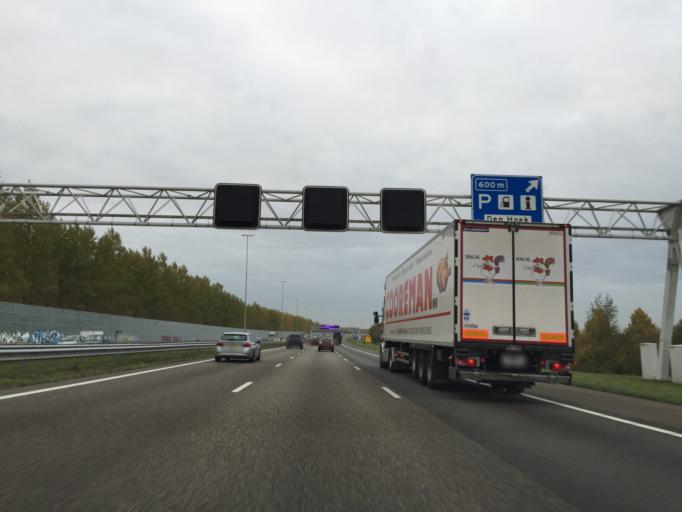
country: NL
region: North Brabant
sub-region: Gemeente Made en Drimmelen
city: Made
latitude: 51.6732
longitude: 4.6719
